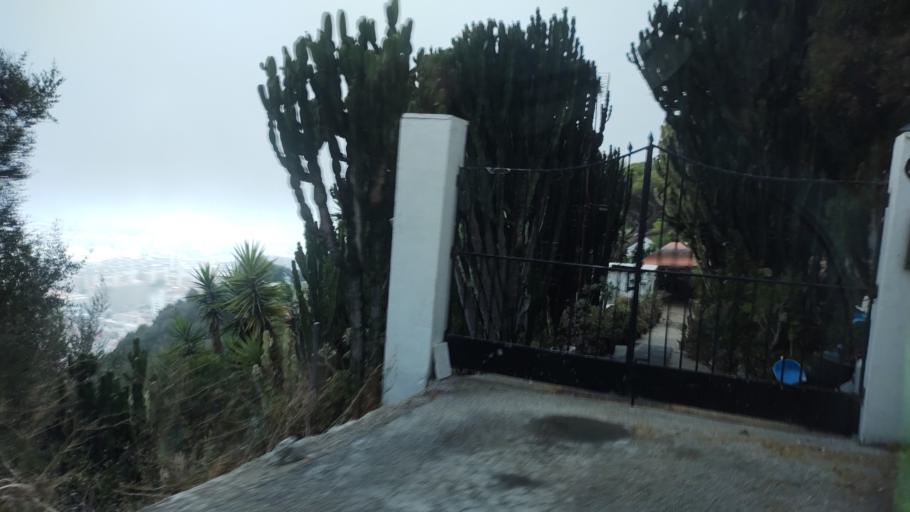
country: GI
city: Gibraltar
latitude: 36.1394
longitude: -5.3479
